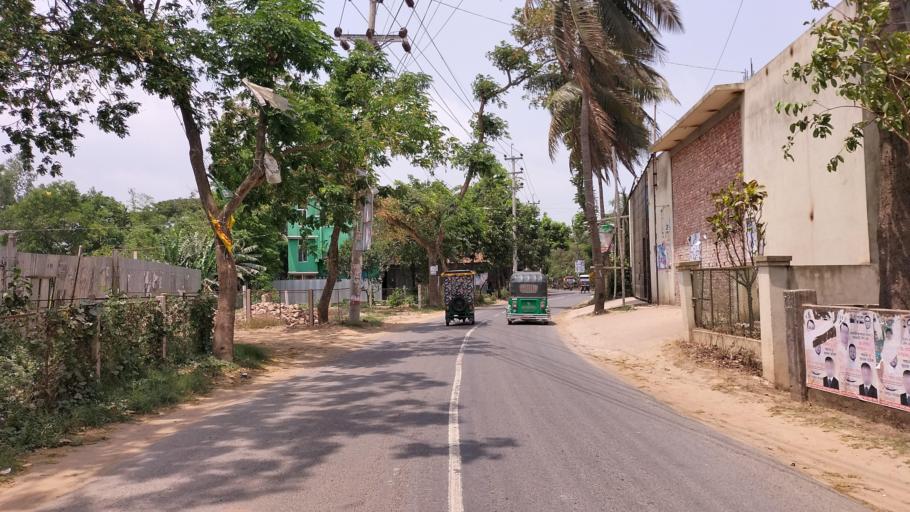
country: BD
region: Dhaka
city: Azimpur
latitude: 23.7285
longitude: 90.2936
